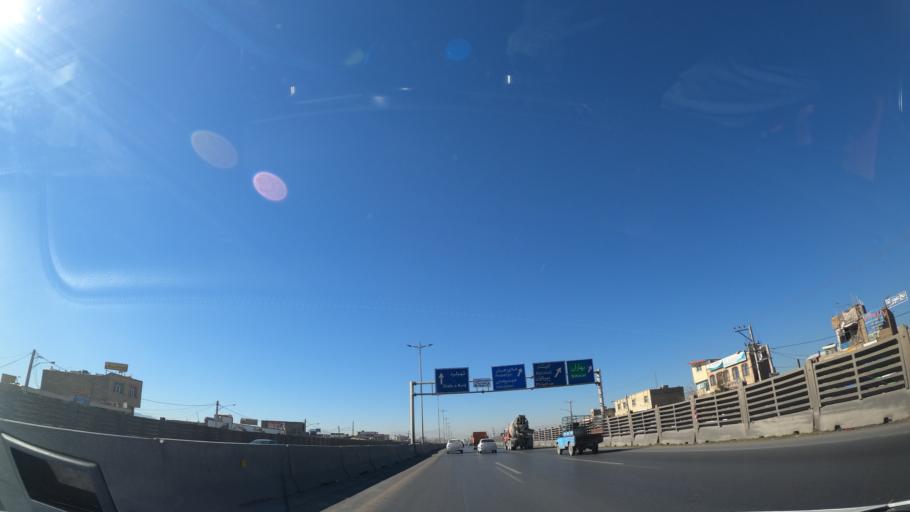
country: IR
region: Isfahan
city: Kelishad va Sudarjan
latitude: 32.5669
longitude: 51.5337
